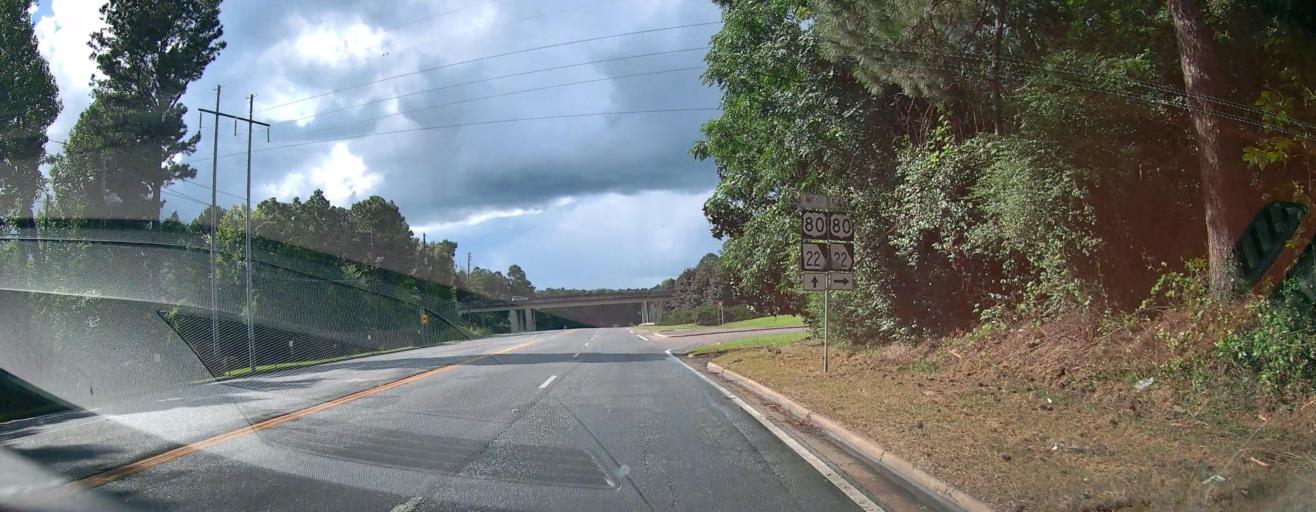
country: US
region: Alabama
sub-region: Russell County
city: Phenix City
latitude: 32.5214
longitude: -84.9883
